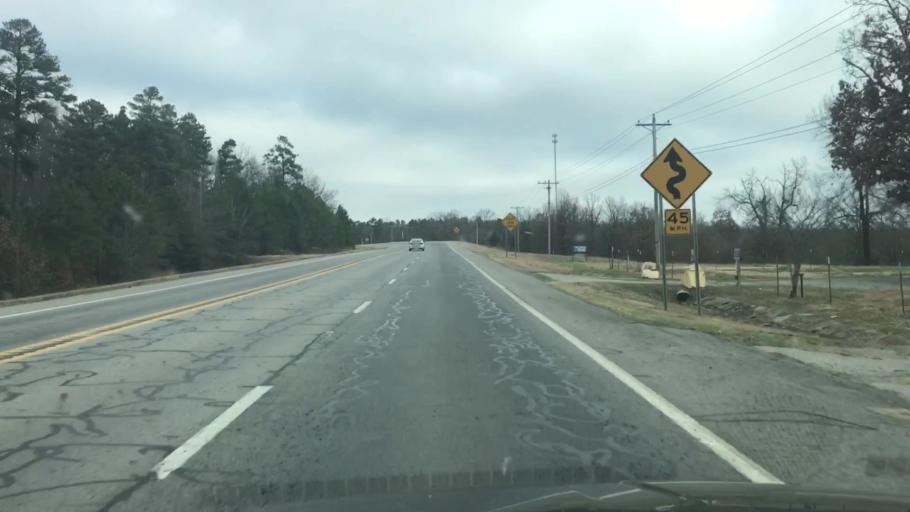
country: US
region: Arkansas
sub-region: Scott County
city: Waldron
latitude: 34.8159
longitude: -94.0386
